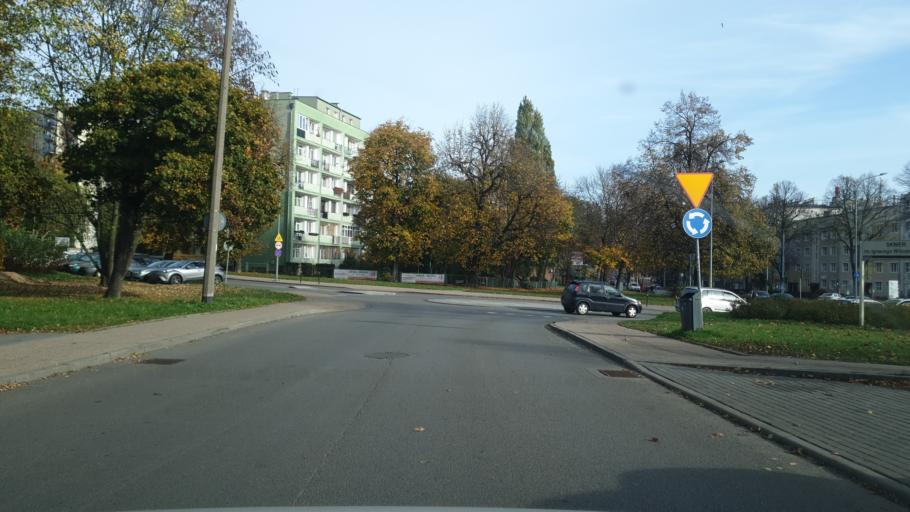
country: PL
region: Pomeranian Voivodeship
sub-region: Gdansk
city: Gdansk
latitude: 54.3510
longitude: 18.6321
